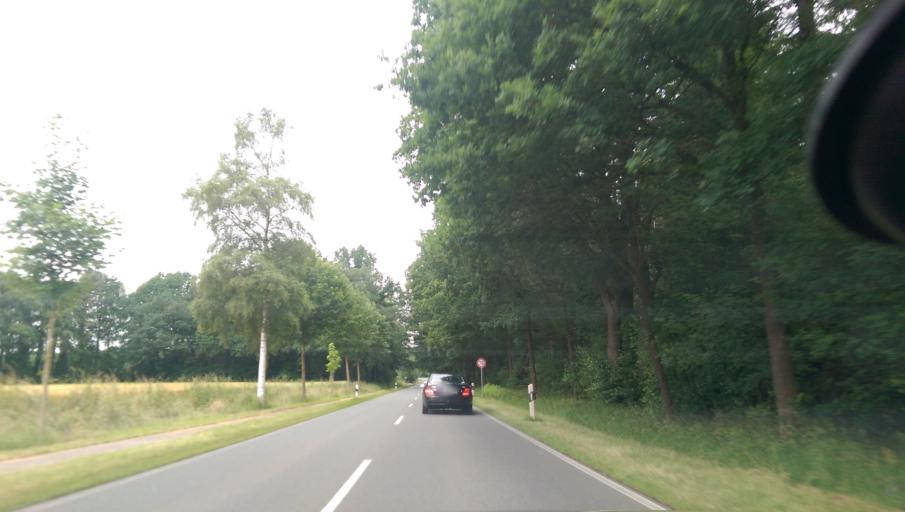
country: DE
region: Lower Saxony
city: Bad Fallingbostel
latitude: 52.8872
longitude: 9.6924
